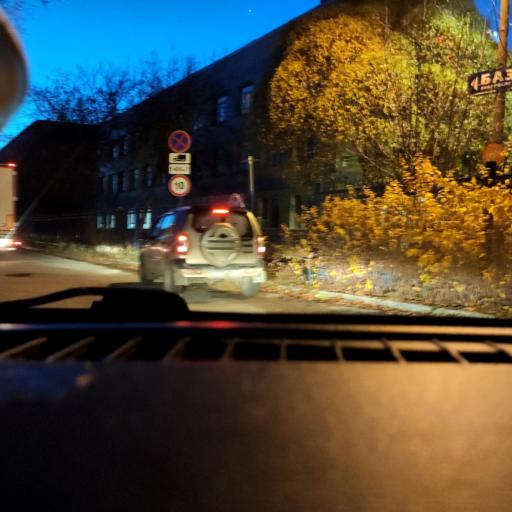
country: RU
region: Perm
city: Kondratovo
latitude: 58.0220
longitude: 56.1646
